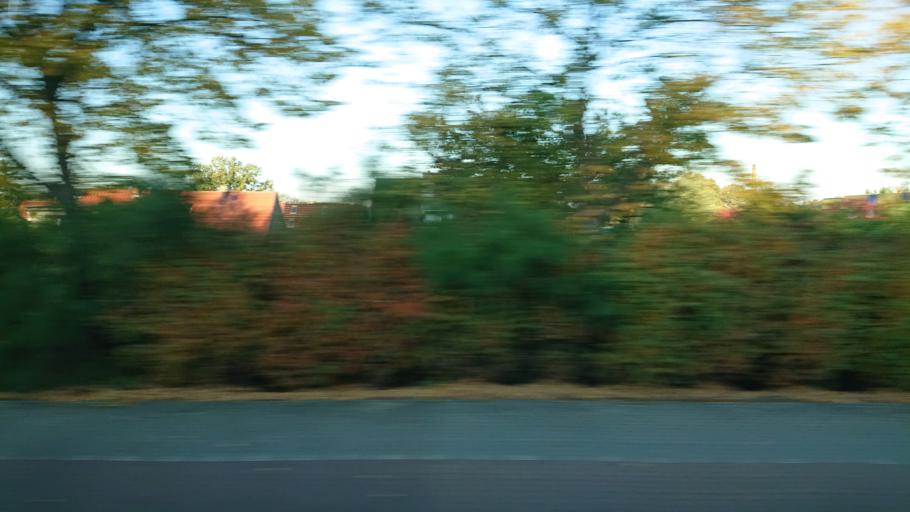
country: DE
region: Mecklenburg-Vorpommern
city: Neubrandenburg
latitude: 53.5771
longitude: 13.2696
